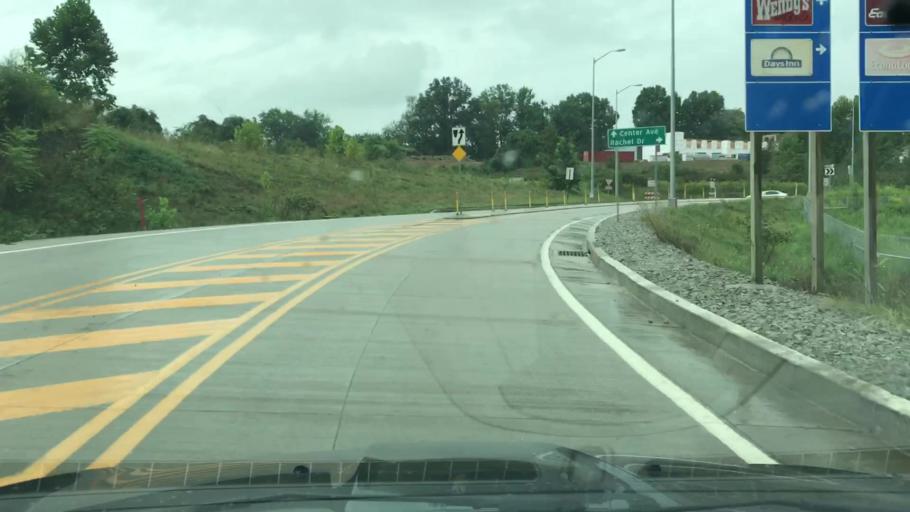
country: US
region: Pennsylvania
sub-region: Westmoreland County
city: New Stanton
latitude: 40.2171
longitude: -79.6144
